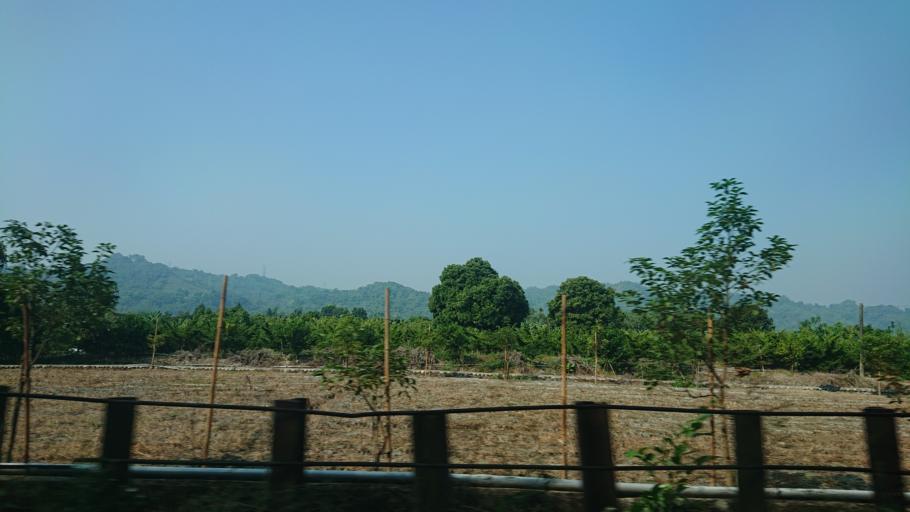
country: TW
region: Taiwan
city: Lugu
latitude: 23.7052
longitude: 120.6632
